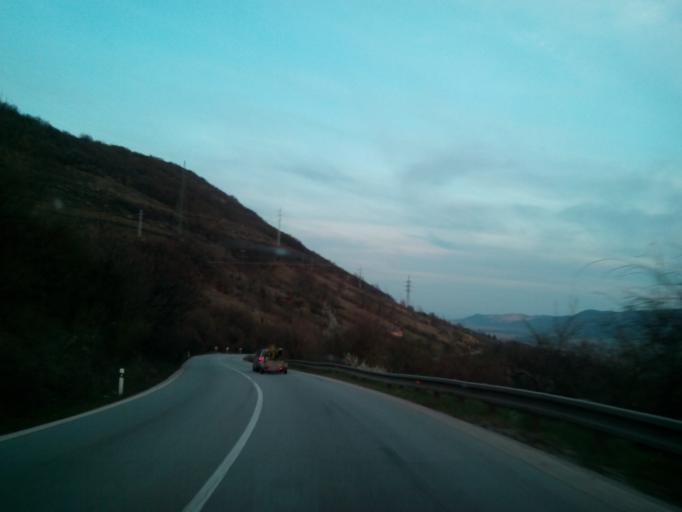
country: SK
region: Kosicky
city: Roznava
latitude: 48.6004
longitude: 20.6538
